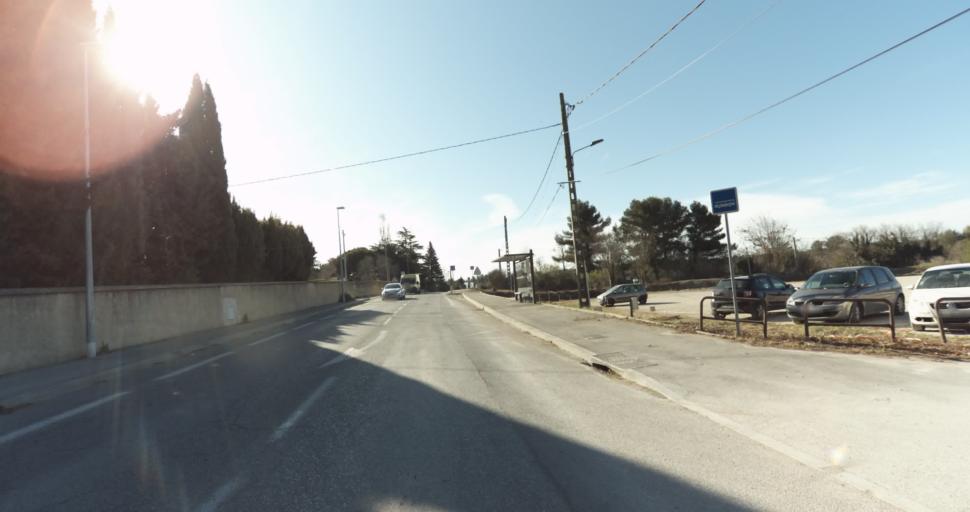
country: FR
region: Provence-Alpes-Cote d'Azur
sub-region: Departement des Bouches-du-Rhone
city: Aix-en-Provence
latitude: 43.5743
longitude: 5.4224
